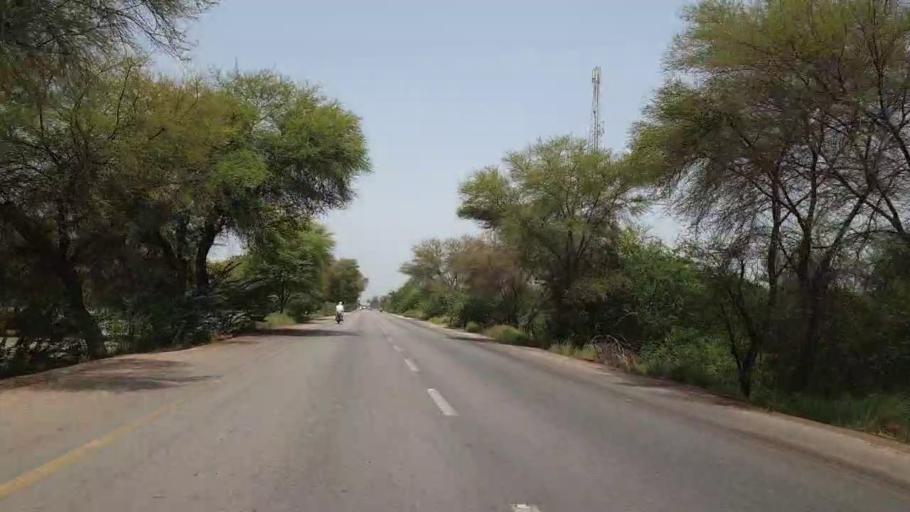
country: PK
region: Sindh
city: Nawabshah
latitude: 26.2110
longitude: 68.5196
